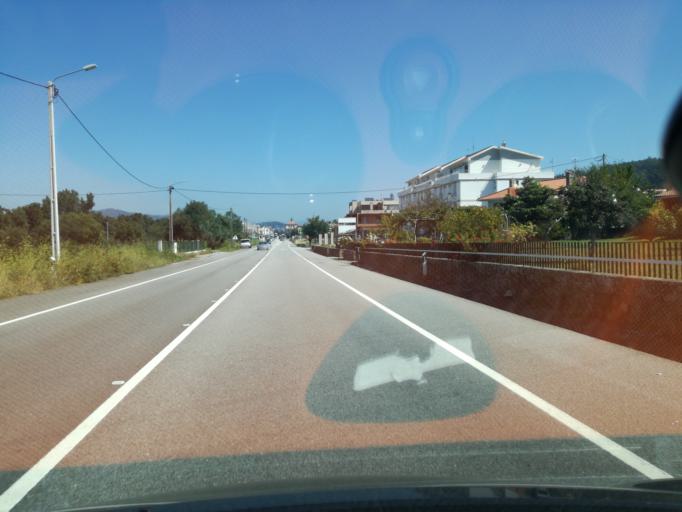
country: ES
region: Galicia
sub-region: Provincia de Pontevedra
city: O Rosal
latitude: 41.8912
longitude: -8.8219
